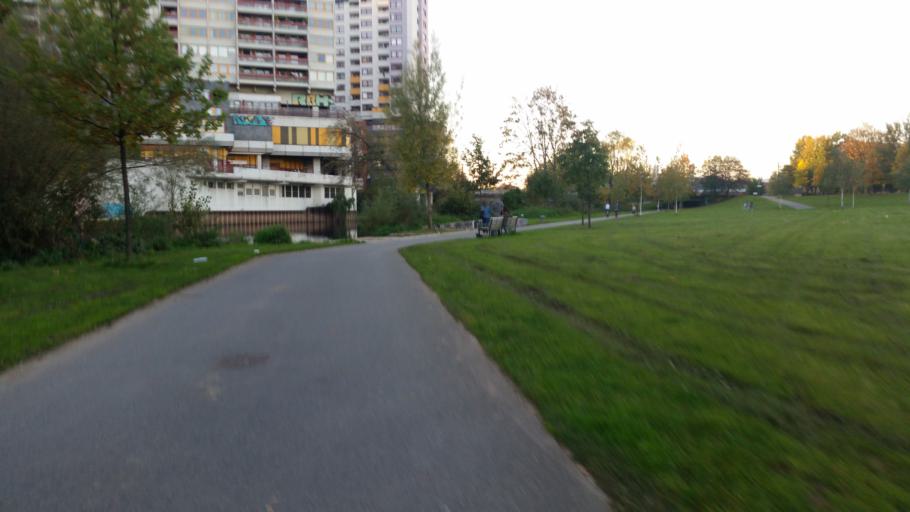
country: DE
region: Lower Saxony
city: Hannover
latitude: 52.3711
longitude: 9.7188
